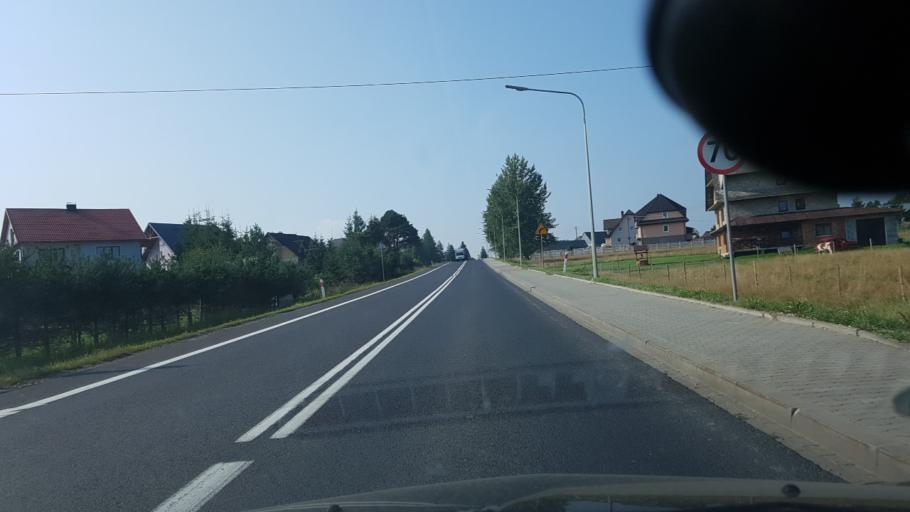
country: PL
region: Lesser Poland Voivodeship
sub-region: Powiat nowotarski
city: Jablonka
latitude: 49.4612
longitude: 19.6907
